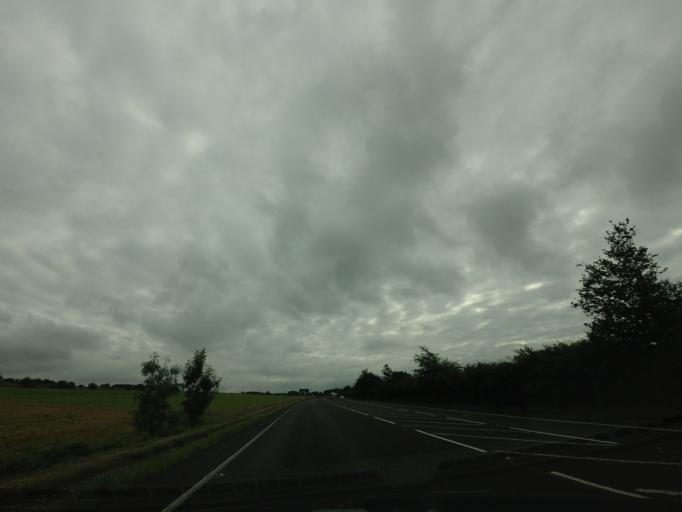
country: GB
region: Scotland
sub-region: Dumfries and Galloway
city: Gretna
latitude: 54.9957
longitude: -3.0913
